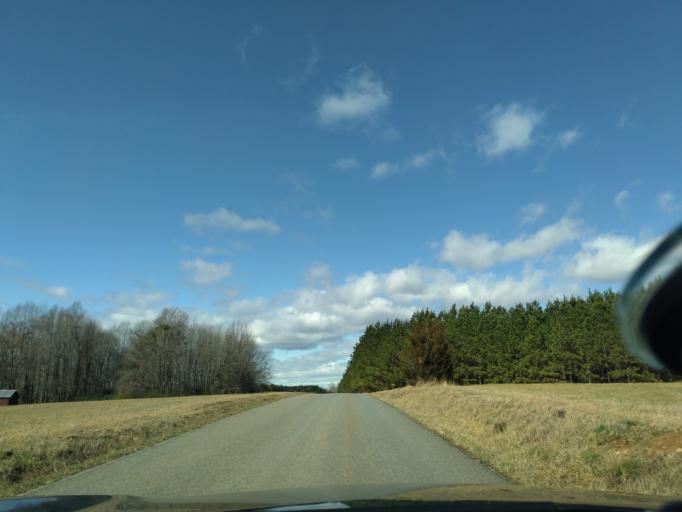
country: US
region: Virginia
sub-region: Nottoway County
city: Crewe
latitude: 37.1698
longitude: -78.2538
